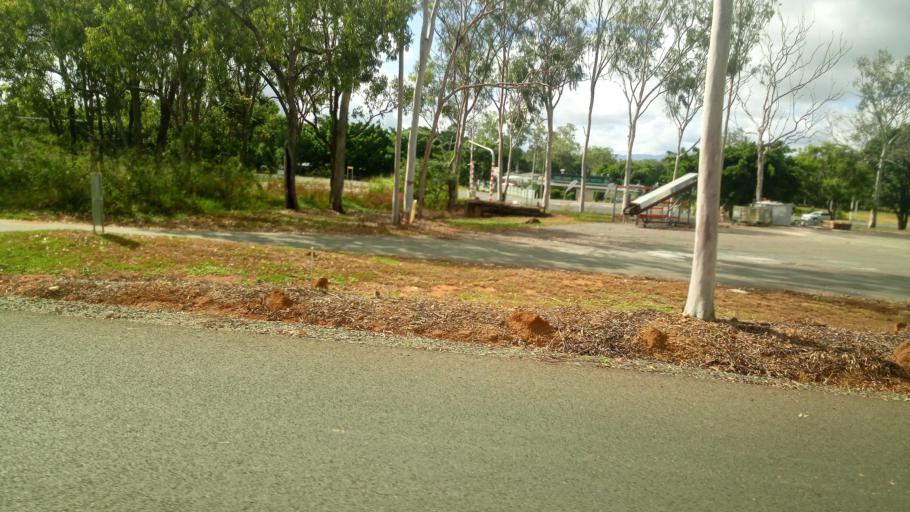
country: AU
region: Queensland
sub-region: Tablelands
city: Mareeba
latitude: -16.9727
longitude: 145.4143
